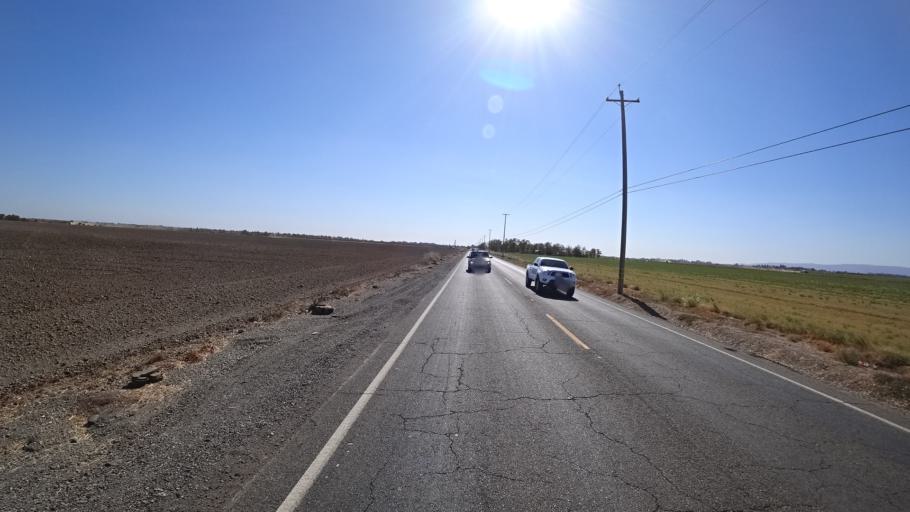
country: US
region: California
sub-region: Yolo County
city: Davis
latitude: 38.5731
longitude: -121.8032
